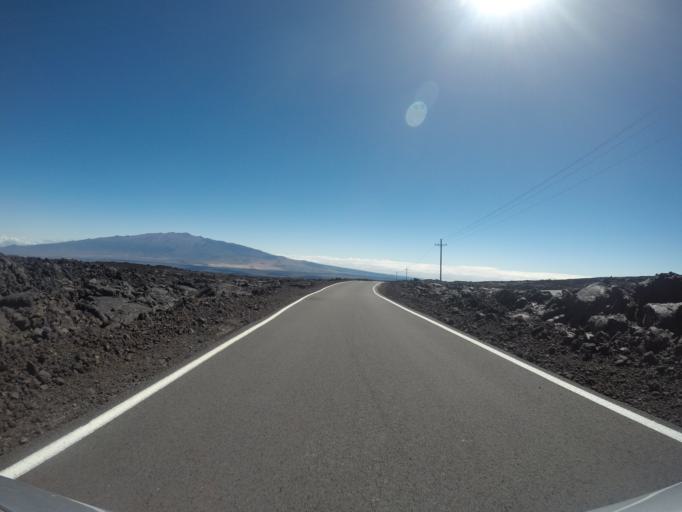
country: US
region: Hawaii
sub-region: Hawaii County
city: Volcano
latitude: 19.5588
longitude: -155.5311
